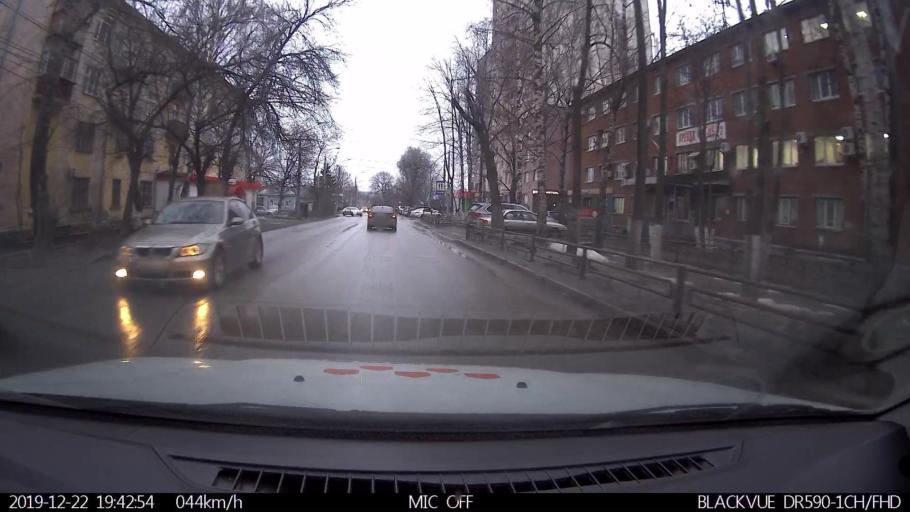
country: RU
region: Nizjnij Novgorod
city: Nizhniy Novgorod
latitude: 56.3114
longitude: 44.0363
